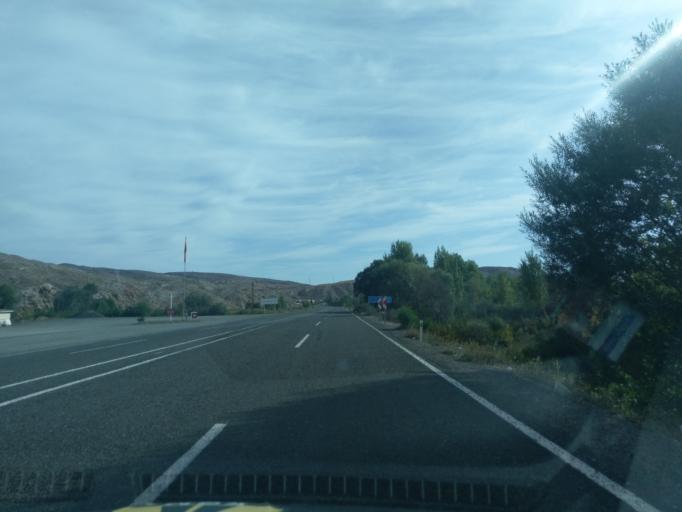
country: TR
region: Sivas
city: Zara
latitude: 39.8539
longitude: 37.8628
